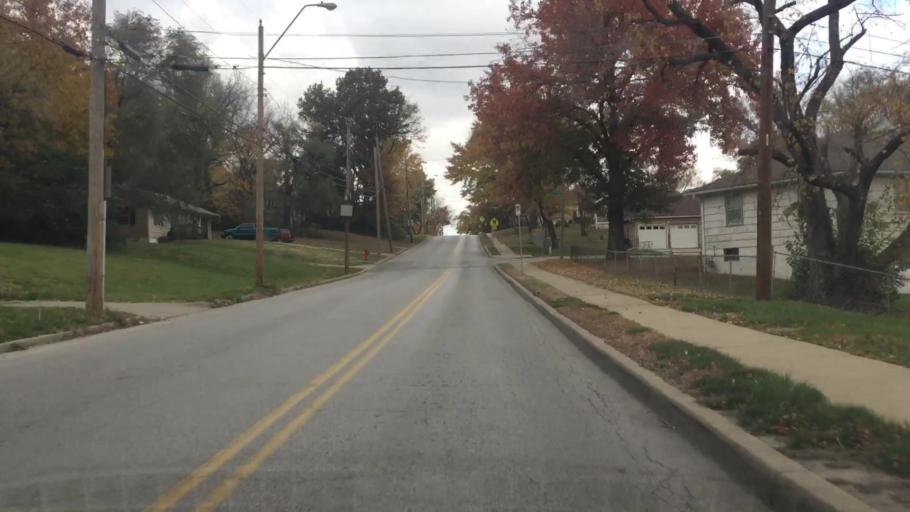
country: US
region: Kansas
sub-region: Johnson County
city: Mission Hills
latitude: 38.9942
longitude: -94.5431
